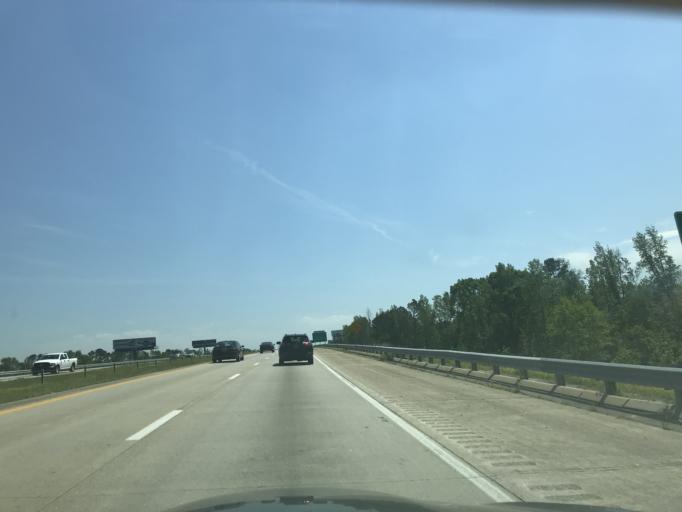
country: US
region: North Carolina
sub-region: Johnston County
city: Benson
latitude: 35.4108
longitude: -78.5245
